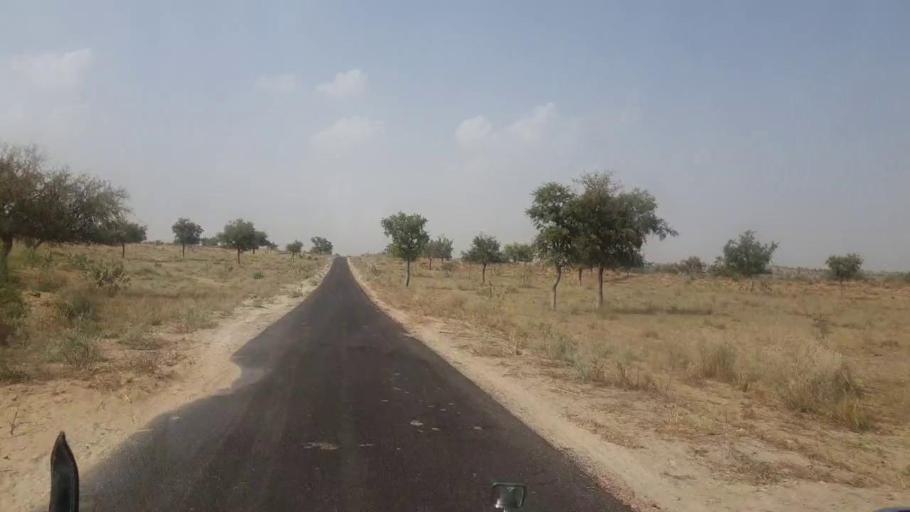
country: PK
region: Sindh
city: Islamkot
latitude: 25.1772
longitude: 70.2879
